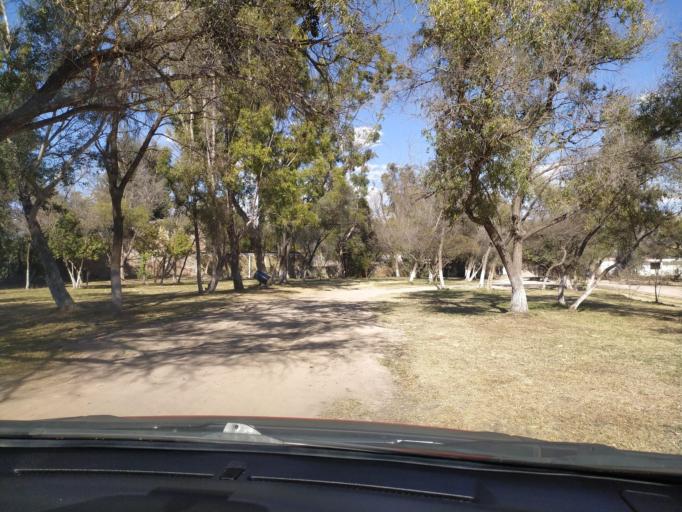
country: LA
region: Oudomxai
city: Muang La
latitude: 21.0465
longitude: 101.8365
